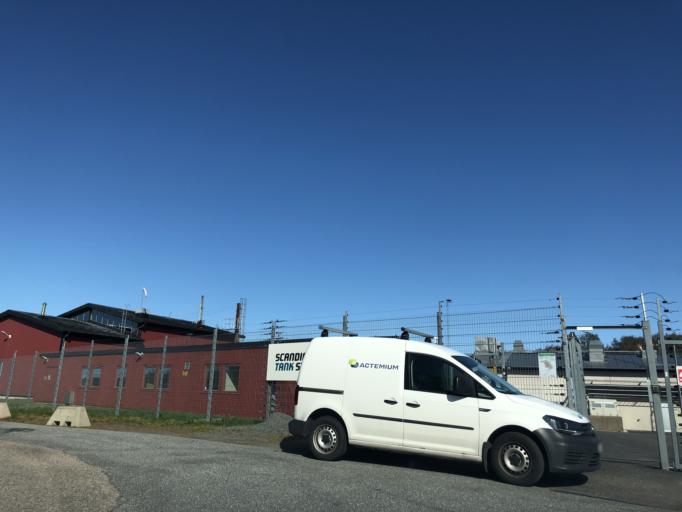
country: SE
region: Vaestra Goetaland
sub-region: Goteborg
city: Torslanda
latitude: 57.7107
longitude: 11.8048
